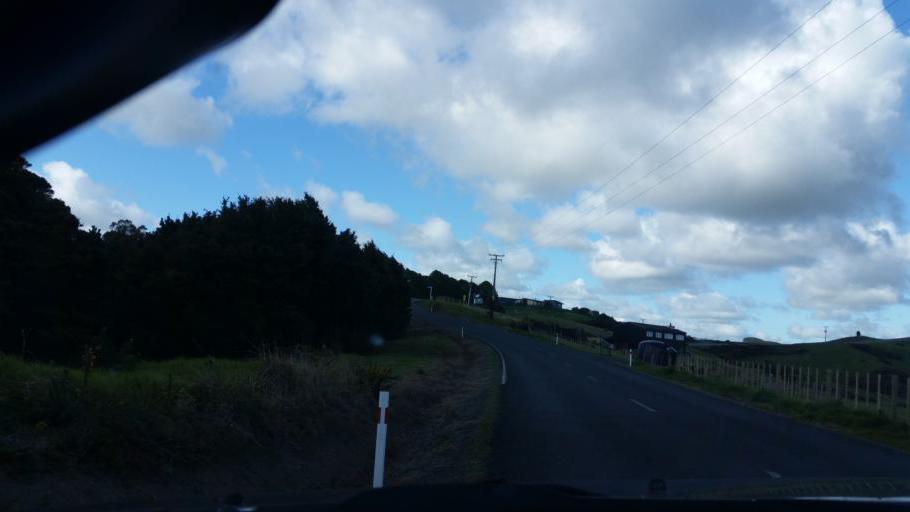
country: NZ
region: Auckland
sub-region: Auckland
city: Wellsford
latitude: -36.1530
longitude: 174.5427
